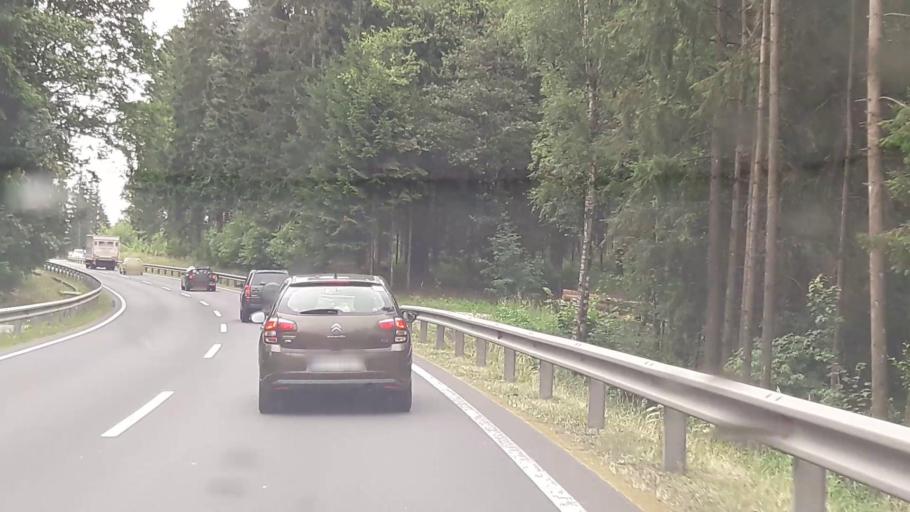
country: AT
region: Upper Austria
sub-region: Politischer Bezirk Rohrbach
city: Kleinzell im Muehlkreis
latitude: 48.4461
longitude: 14.0405
